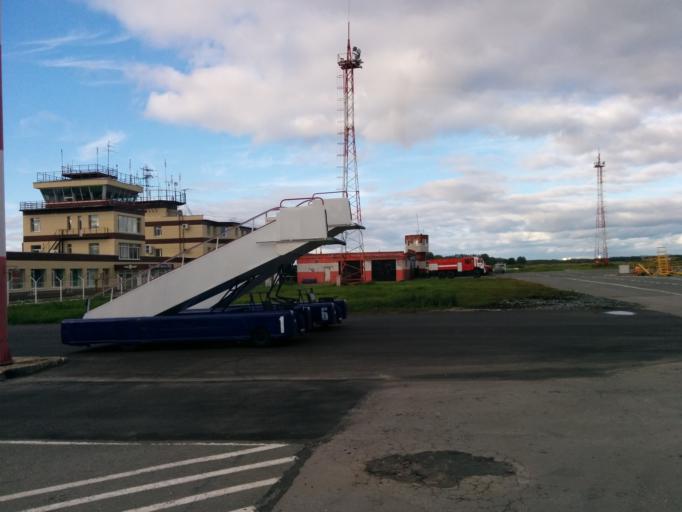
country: RU
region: Perm
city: Kultayevo
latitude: 57.9198
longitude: 56.0205
